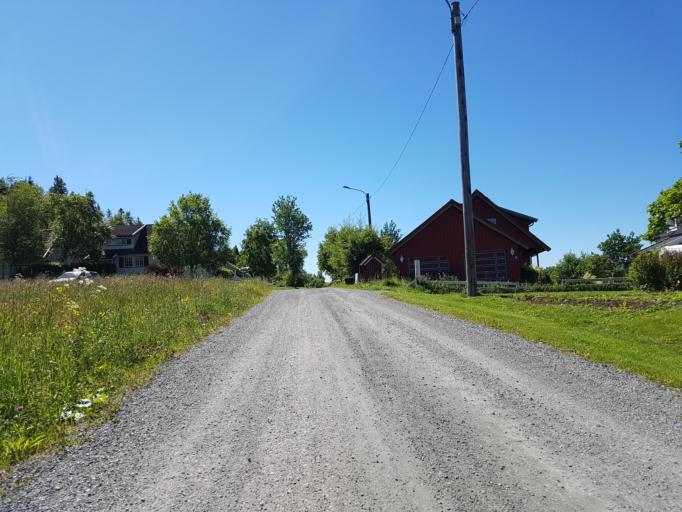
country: NO
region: Sor-Trondelag
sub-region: Skaun
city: Borsa
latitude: 63.4328
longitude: 10.1848
